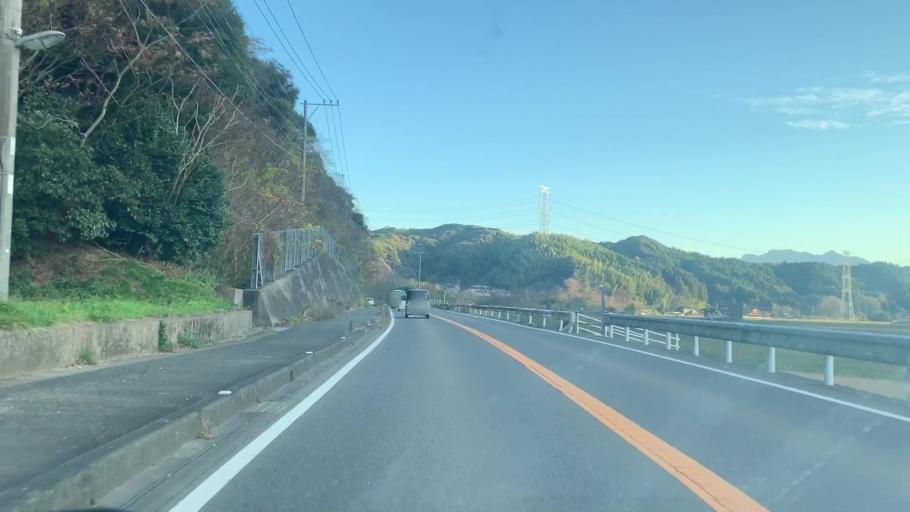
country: JP
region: Saga Prefecture
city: Karatsu
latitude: 33.3654
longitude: 130.0063
